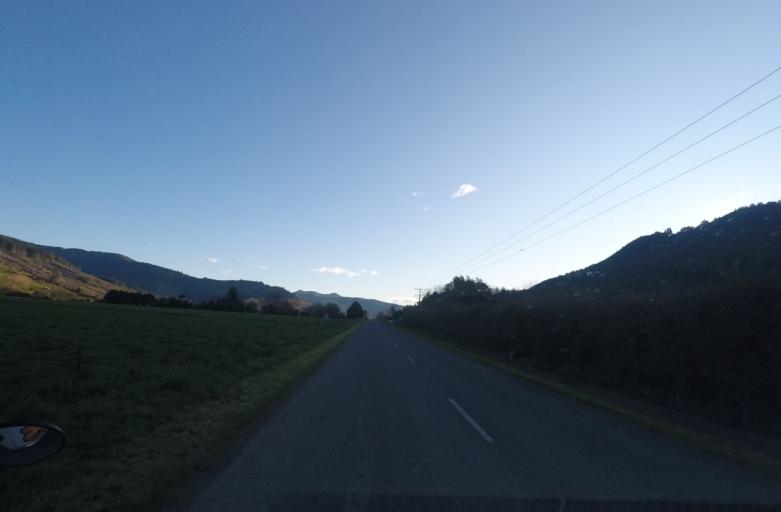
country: NZ
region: Marlborough
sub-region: Marlborough District
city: Picton
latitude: -41.2903
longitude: 173.8887
